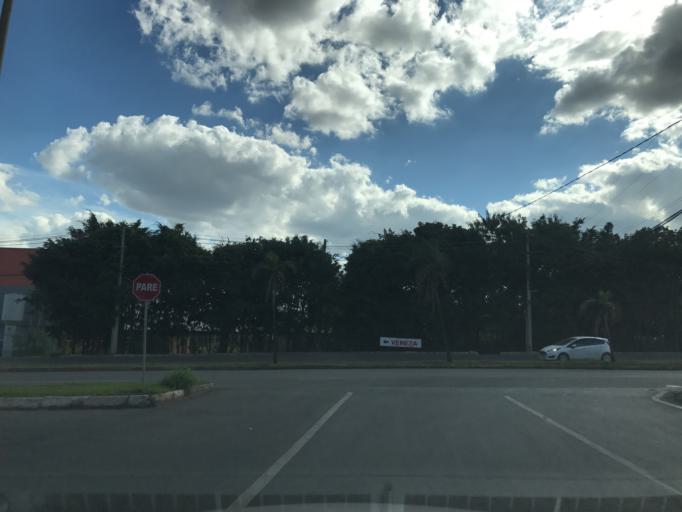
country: BR
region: Federal District
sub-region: Brasilia
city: Brasilia
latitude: -15.8020
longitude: -47.9711
